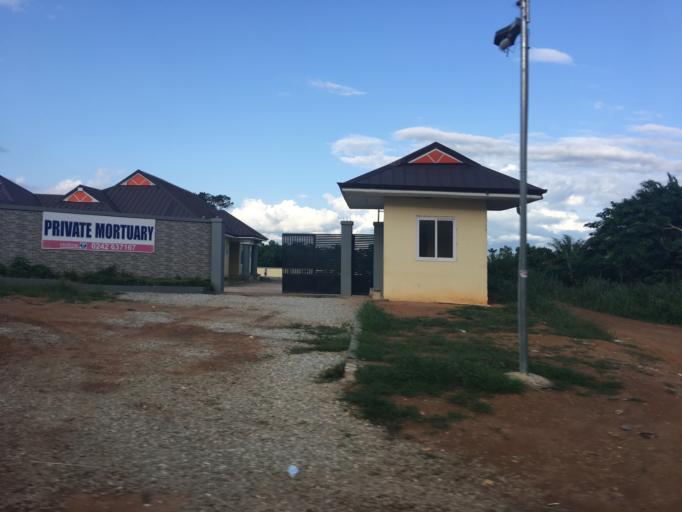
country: GH
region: Western
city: Bibiani
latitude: 6.3151
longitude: -2.2511
